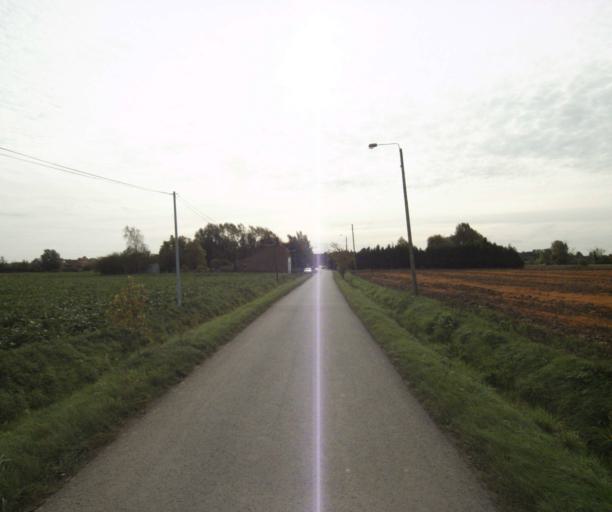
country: FR
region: Nord-Pas-de-Calais
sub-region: Departement du Nord
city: Radinghem-en-Weppes
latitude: 50.6197
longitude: 2.8789
